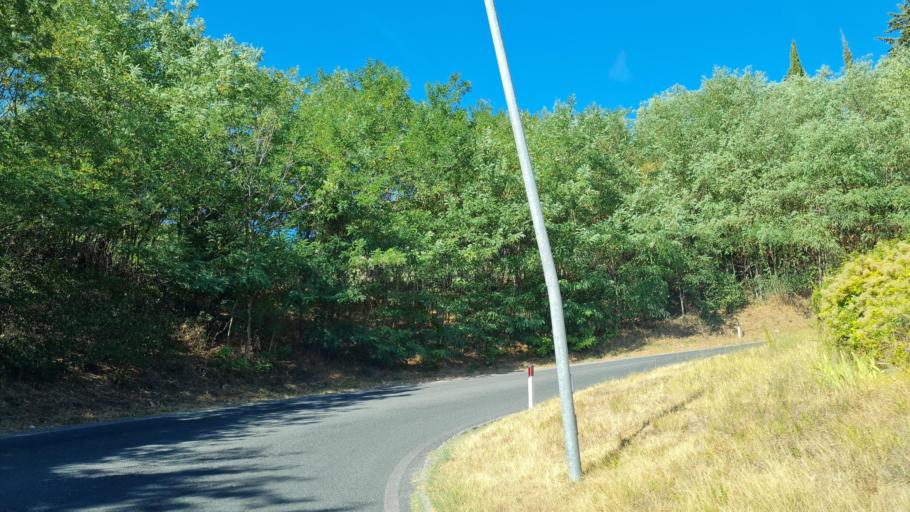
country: IT
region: Tuscany
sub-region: Provincia di Siena
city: Chianciano Terme
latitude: 43.0585
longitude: 11.8212
